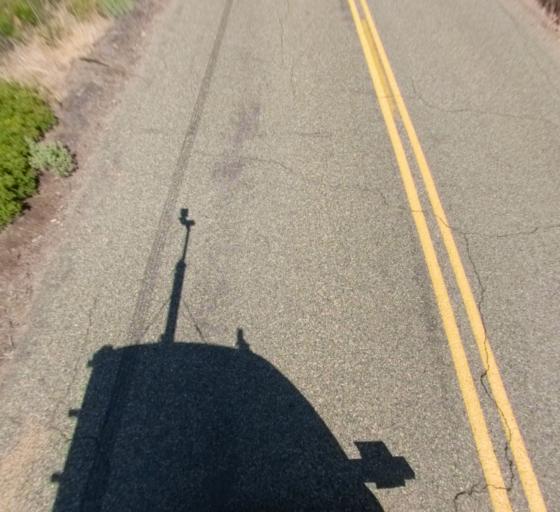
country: US
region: California
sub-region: Fresno County
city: Auberry
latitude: 37.2963
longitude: -119.3520
